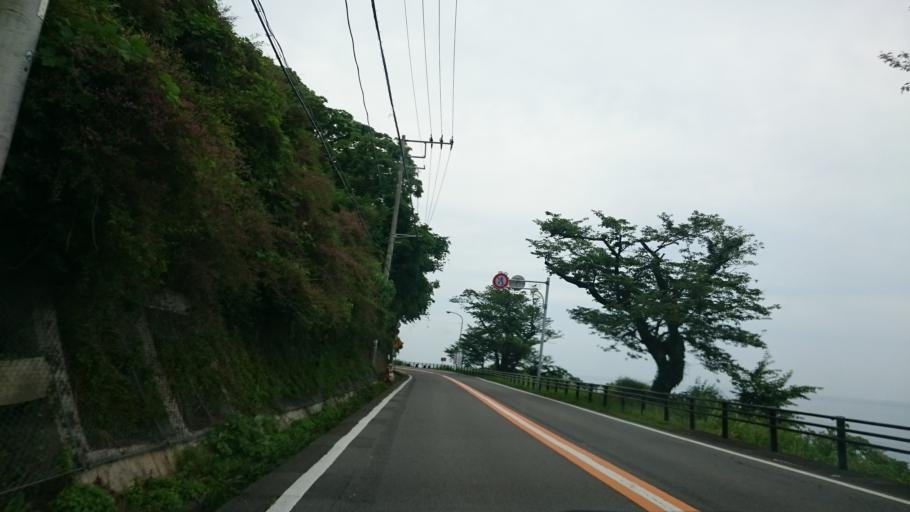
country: JP
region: Shizuoka
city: Ito
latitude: 35.0246
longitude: 139.0977
